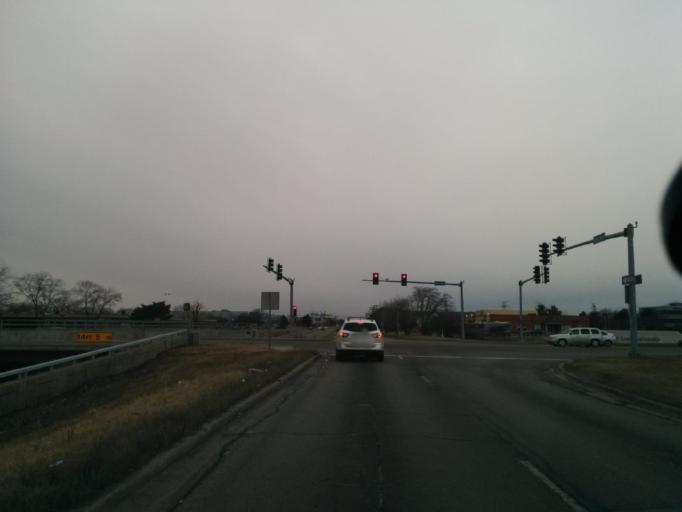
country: US
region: Illinois
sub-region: Cook County
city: Prospect Heights
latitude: 42.1097
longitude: -87.9070
